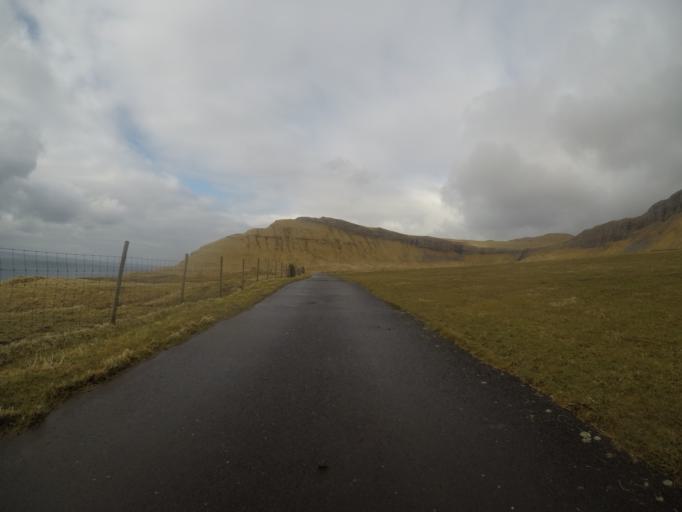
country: FO
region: Streymoy
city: Kollafjordhur
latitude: 62.0402
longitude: -6.9564
